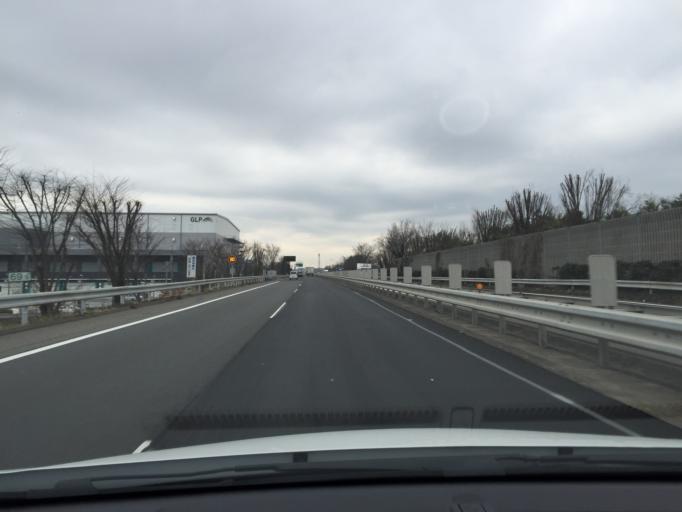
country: JP
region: Saitama
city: Sayama
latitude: 35.8718
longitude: 139.3762
